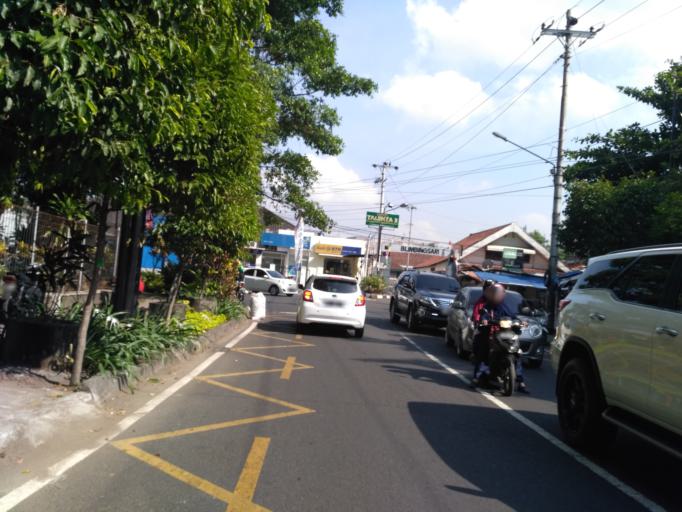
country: ID
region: Daerah Istimewa Yogyakarta
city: Yogyakarta
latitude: -7.7755
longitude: 110.3730
